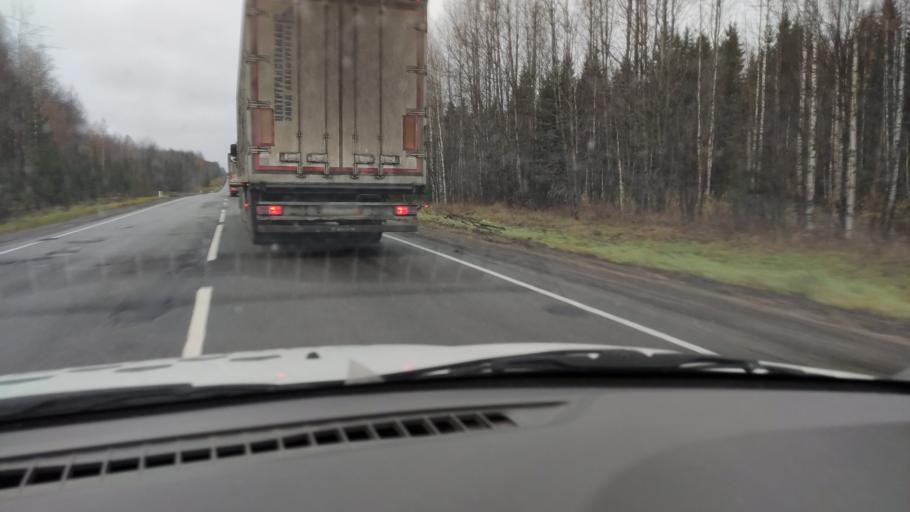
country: RU
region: Kirov
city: Omutninsk
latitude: 58.7546
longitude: 52.0430
